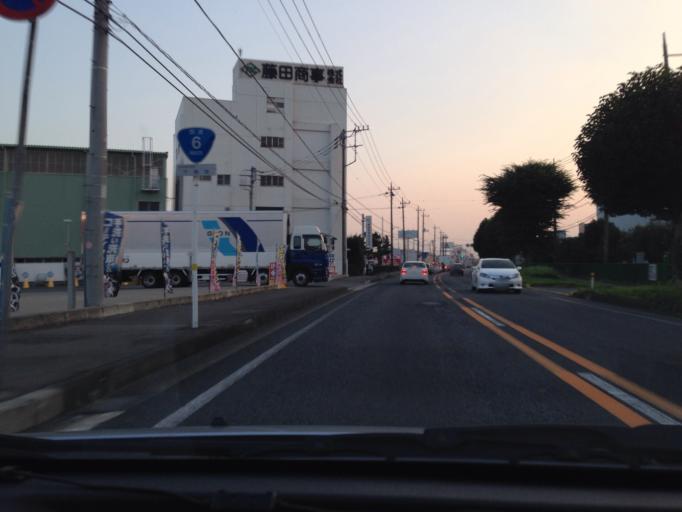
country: JP
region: Ibaraki
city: Ishioka
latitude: 36.1329
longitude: 140.2290
